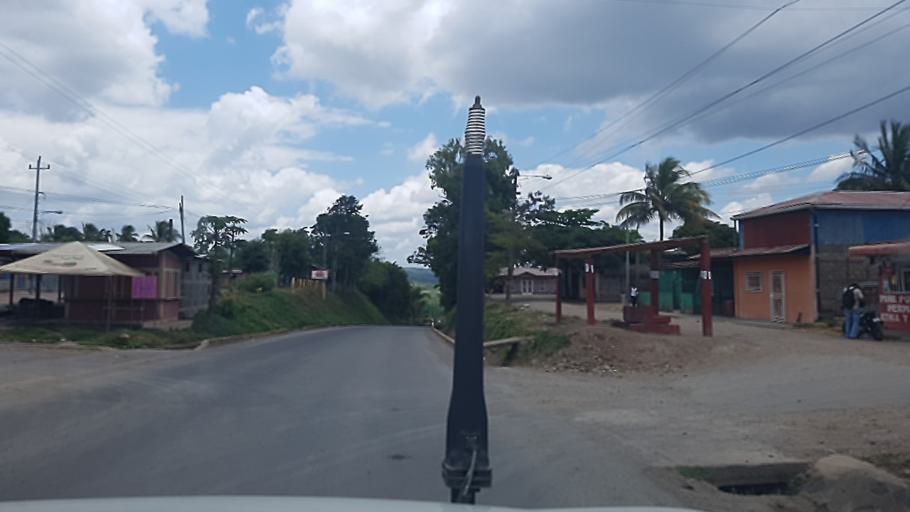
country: NI
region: Chontales
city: Santo Tomas
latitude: 12.0652
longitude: -85.0903
